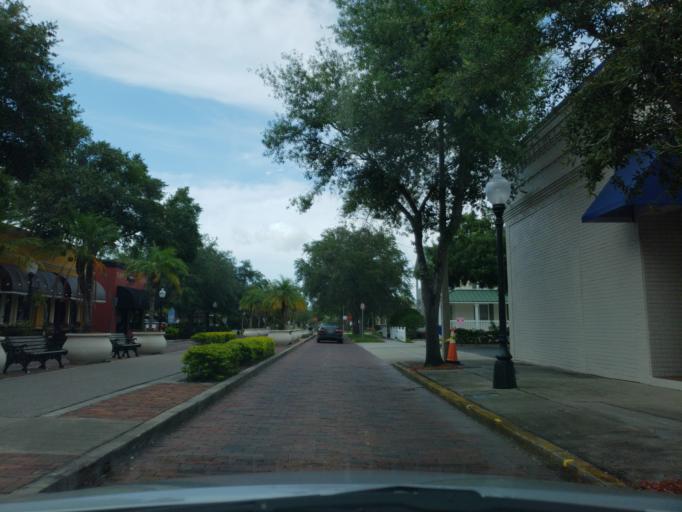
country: US
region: Florida
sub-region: Pinellas County
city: Tarpon Springs
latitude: 28.1464
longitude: -82.7546
